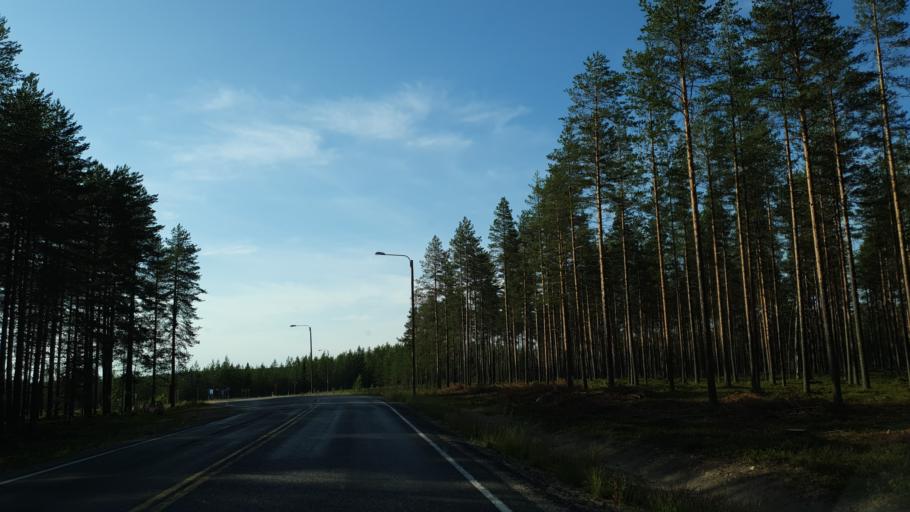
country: FI
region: Kainuu
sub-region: Kehys-Kainuu
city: Kuhmo
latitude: 64.0982
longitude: 29.4753
